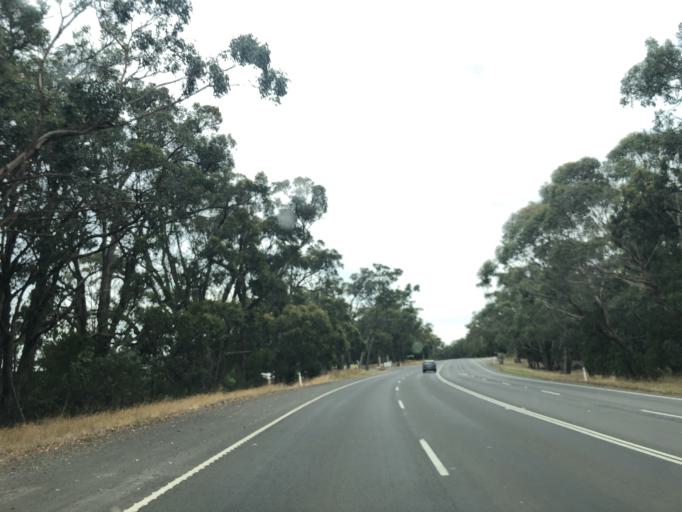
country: AU
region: Victoria
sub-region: Hume
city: Sunbury
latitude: -37.3804
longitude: 144.5277
